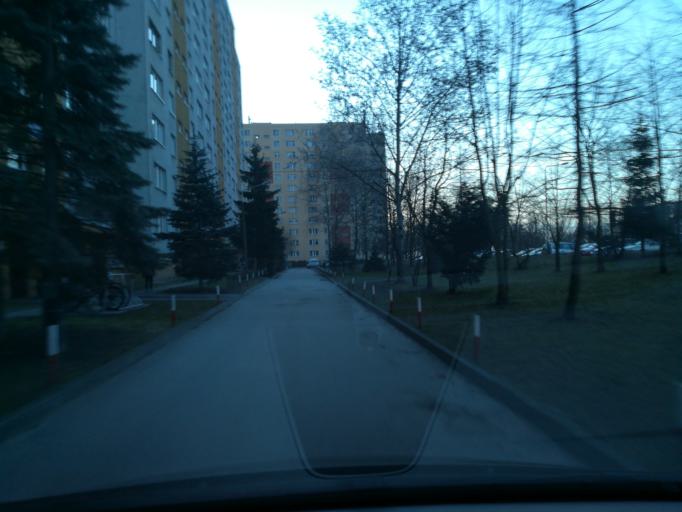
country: PL
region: Lodz Voivodeship
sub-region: Piotrkow Trybunalski
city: Piotrkow Trybunalski
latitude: 51.4100
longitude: 19.6604
